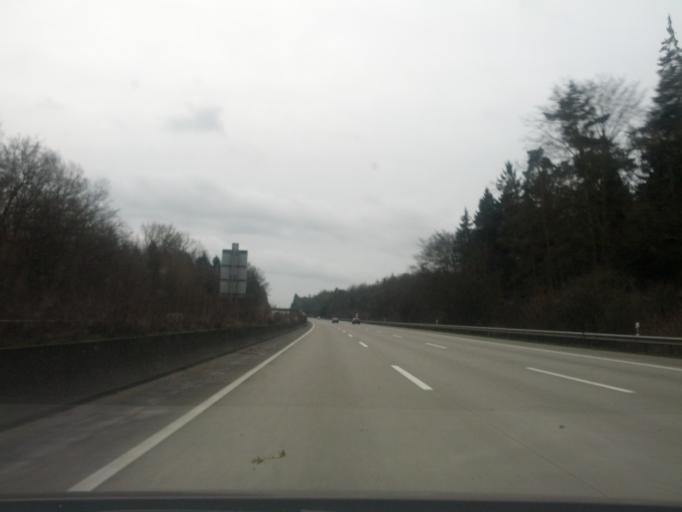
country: DE
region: Lower Saxony
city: Garlstorf
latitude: 53.2213
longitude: 10.0757
